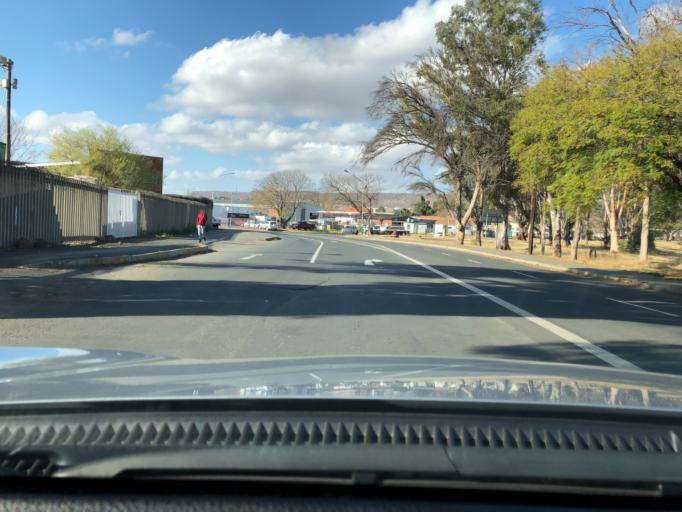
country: ZA
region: KwaZulu-Natal
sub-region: uThukela District Municipality
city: Ladysmith
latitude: -28.5605
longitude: 29.7777
